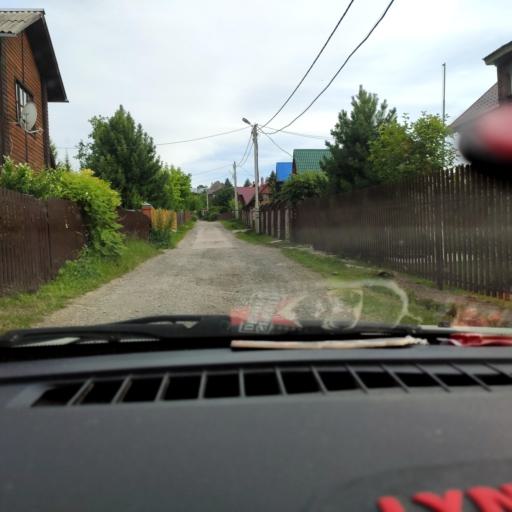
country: RU
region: Perm
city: Polazna
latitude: 58.2495
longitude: 56.2538
